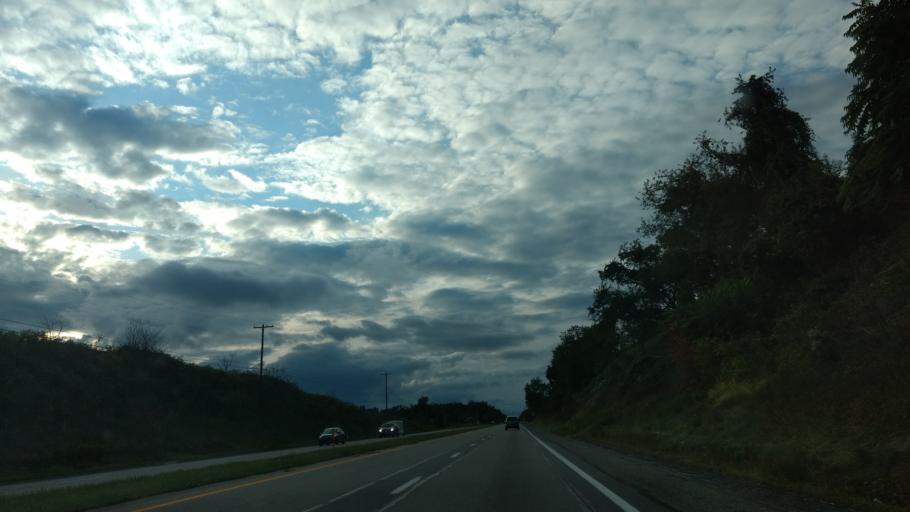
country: US
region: Pennsylvania
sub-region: Westmoreland County
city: Fellsburg
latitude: 40.1689
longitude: -79.7918
